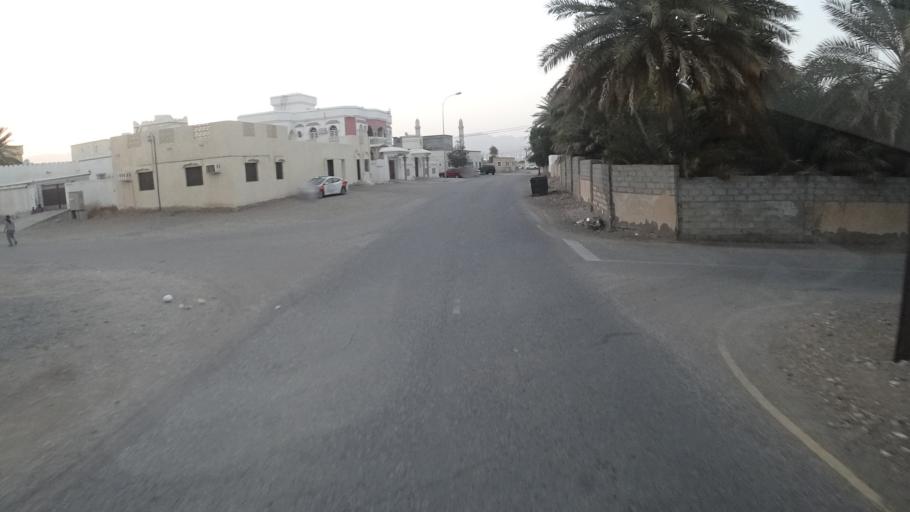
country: OM
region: Ash Sharqiyah
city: Sur
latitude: 22.5423
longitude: 59.4852
